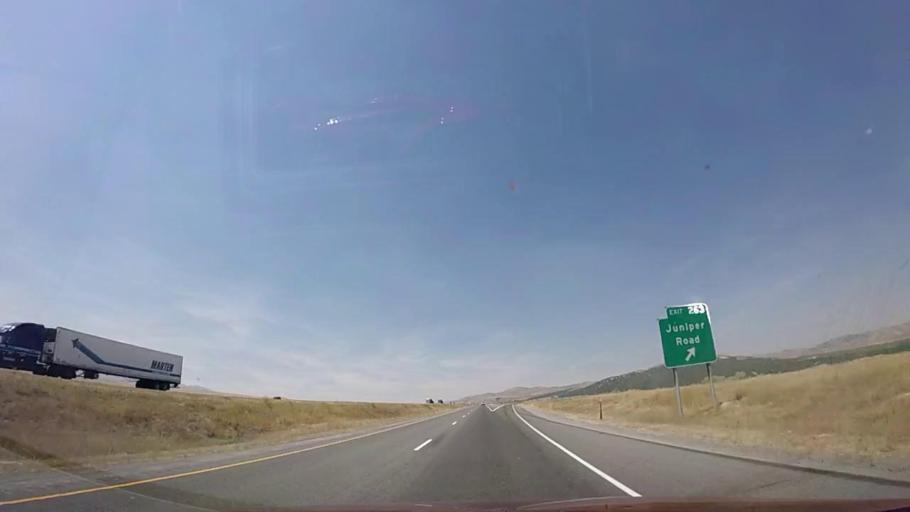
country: US
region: Idaho
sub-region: Power County
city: American Falls
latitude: 42.1470
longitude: -112.9815
